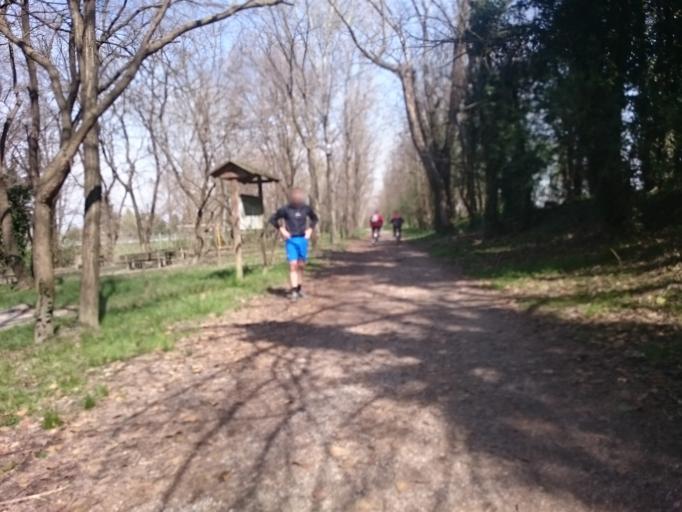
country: IT
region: Veneto
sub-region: Provincia di Padova
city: Limena
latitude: 45.4649
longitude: 11.8364
